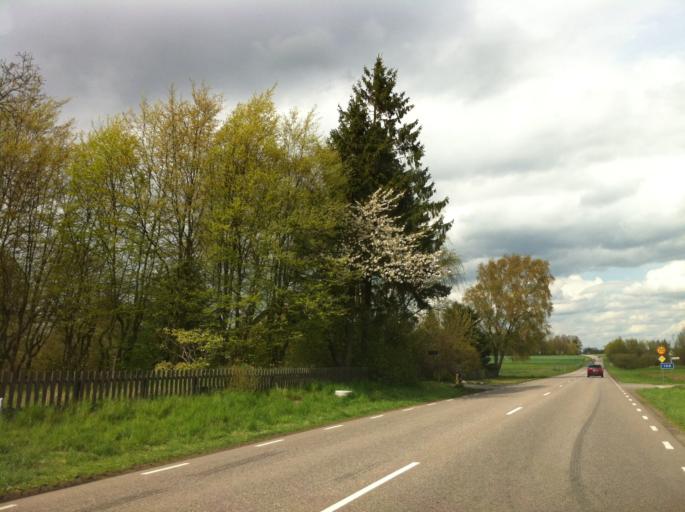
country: SE
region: Skane
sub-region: Kavlinge Kommun
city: Kaevlinge
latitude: 55.8216
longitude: 13.0950
